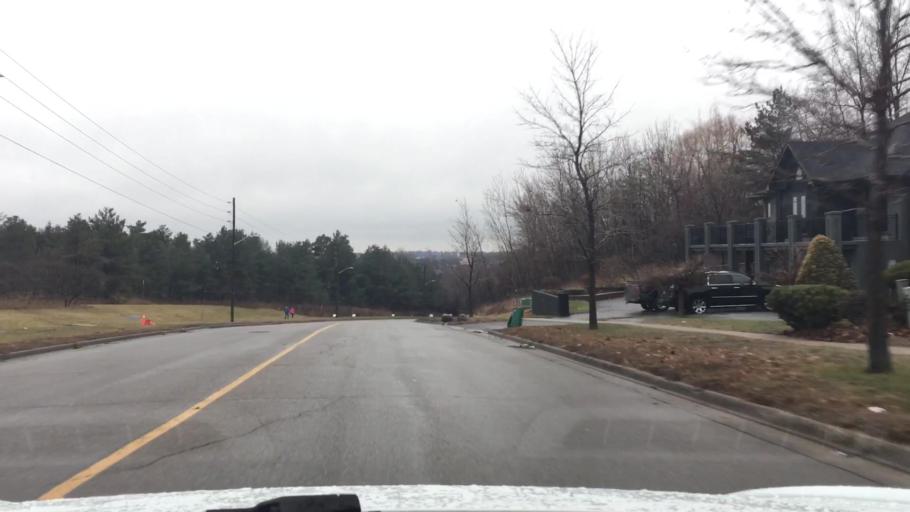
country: CA
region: Ontario
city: Oshawa
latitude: 43.8979
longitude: -78.8146
